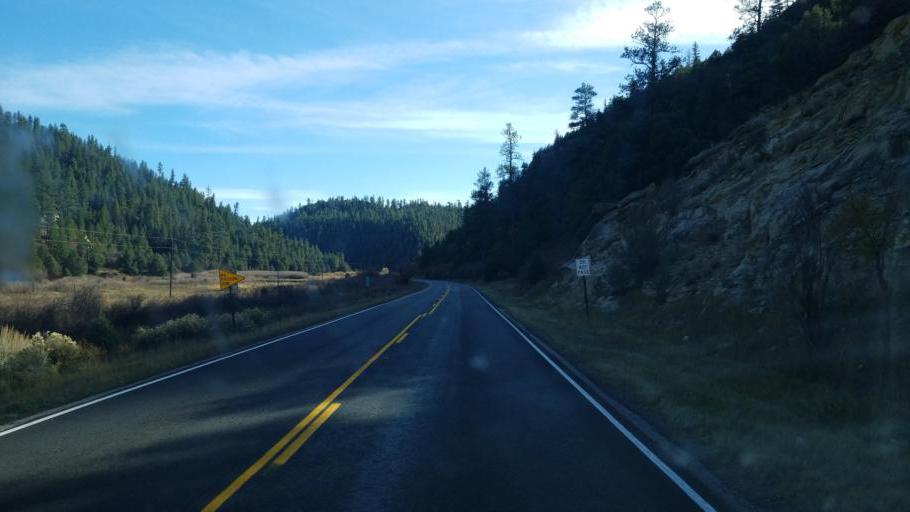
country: US
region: New Mexico
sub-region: Rio Arriba County
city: Dulce
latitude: 36.9017
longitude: -107.0051
